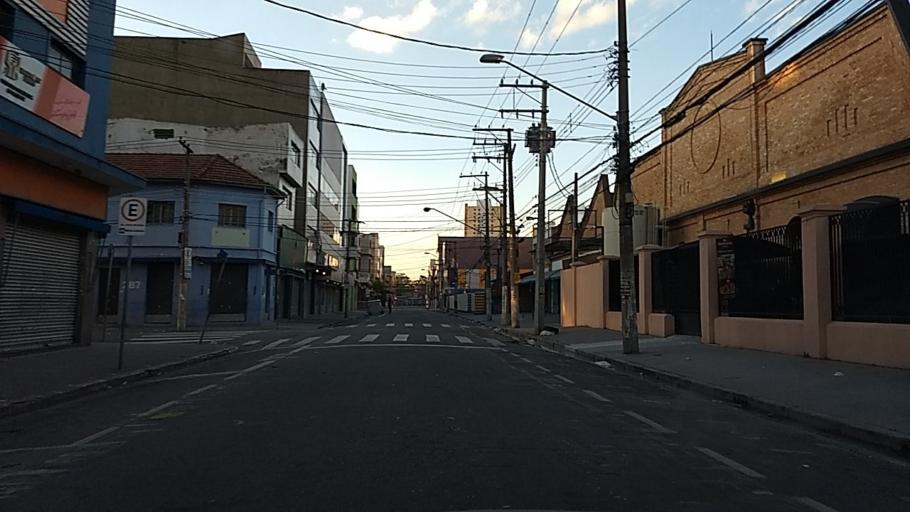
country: BR
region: Sao Paulo
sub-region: Sao Paulo
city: Sao Paulo
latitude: -23.5311
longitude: -46.6202
